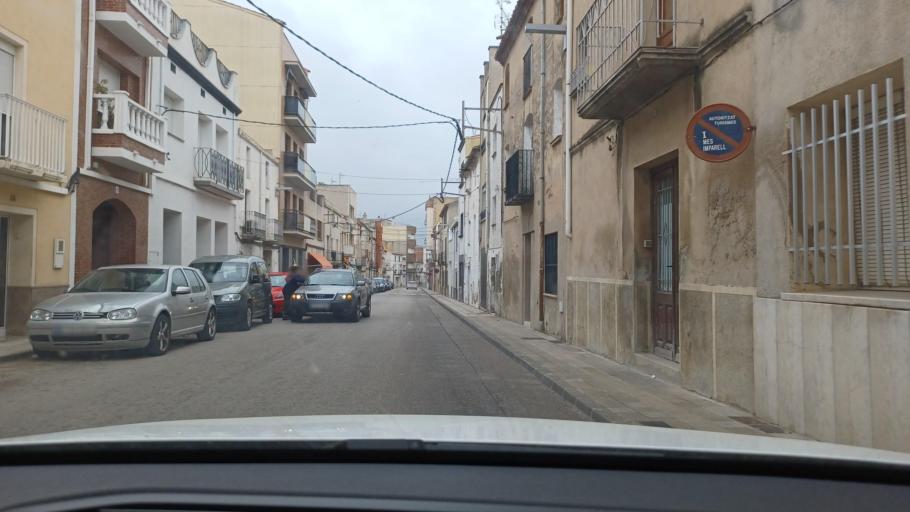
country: ES
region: Catalonia
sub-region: Provincia de Tarragona
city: Tortosa
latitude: 40.8086
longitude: 0.4955
